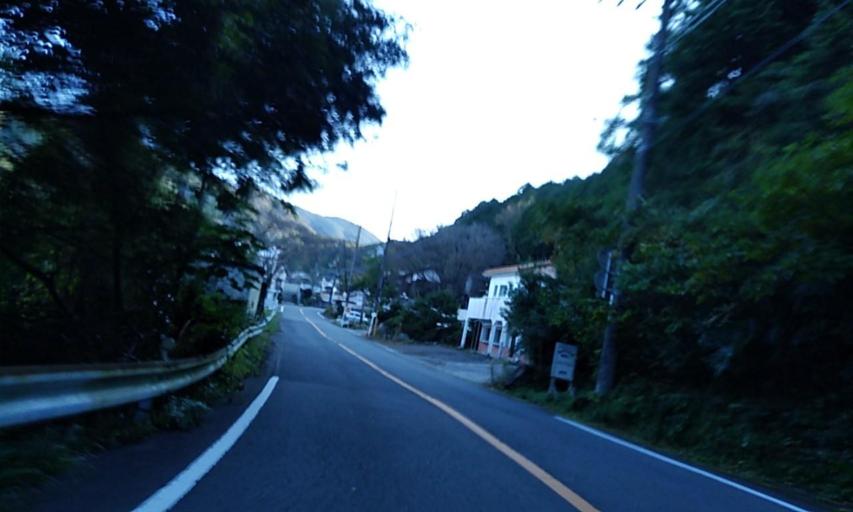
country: JP
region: Wakayama
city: Iwade
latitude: 34.1515
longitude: 135.3164
